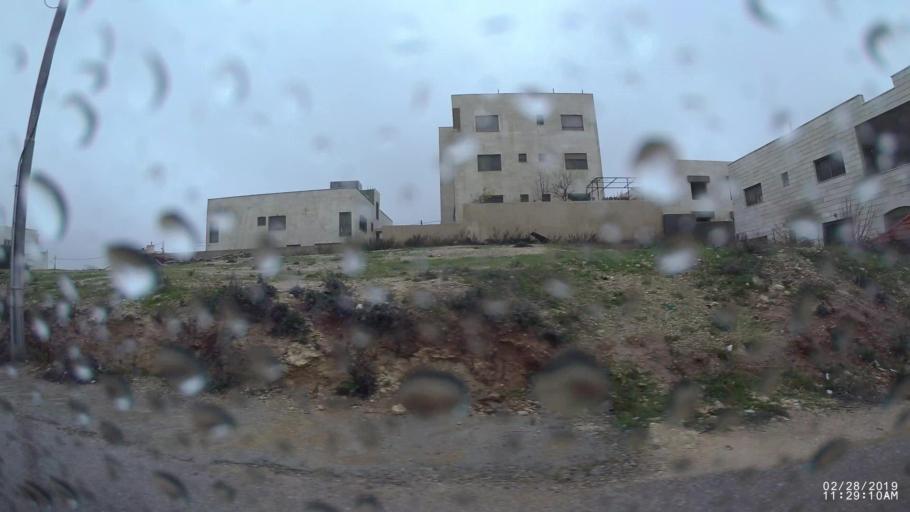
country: JO
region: Amman
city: Al Jubayhah
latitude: 32.0097
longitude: 35.8989
